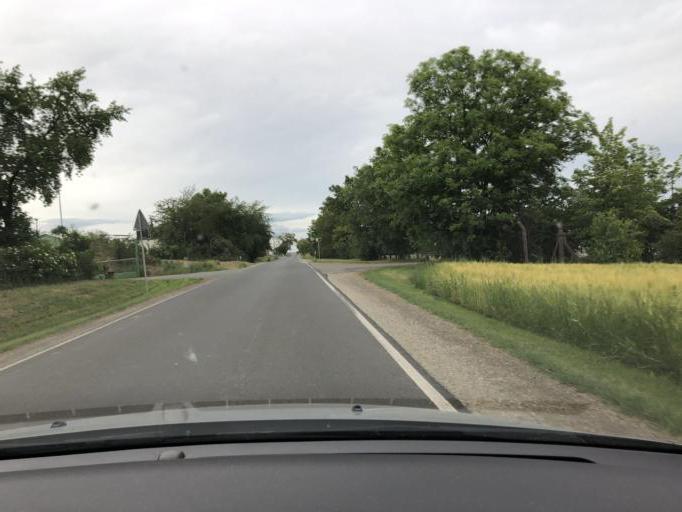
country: DE
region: Thuringia
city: Pfiffelbach
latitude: 51.0654
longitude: 11.4433
